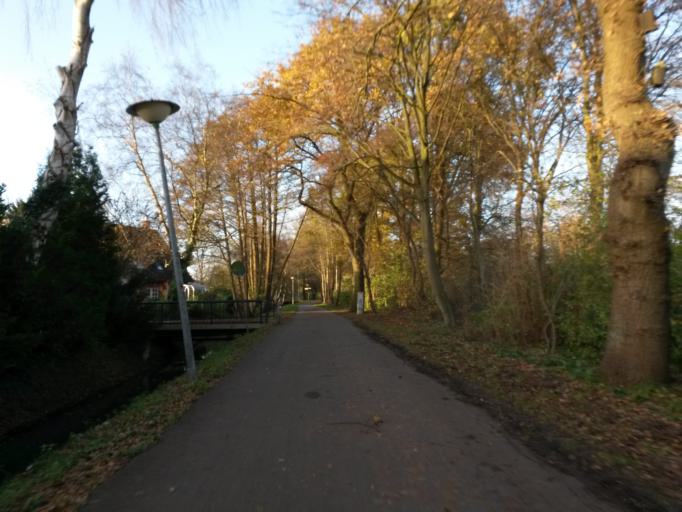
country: DE
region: Lower Saxony
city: Lilienthal
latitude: 53.0748
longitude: 8.9145
